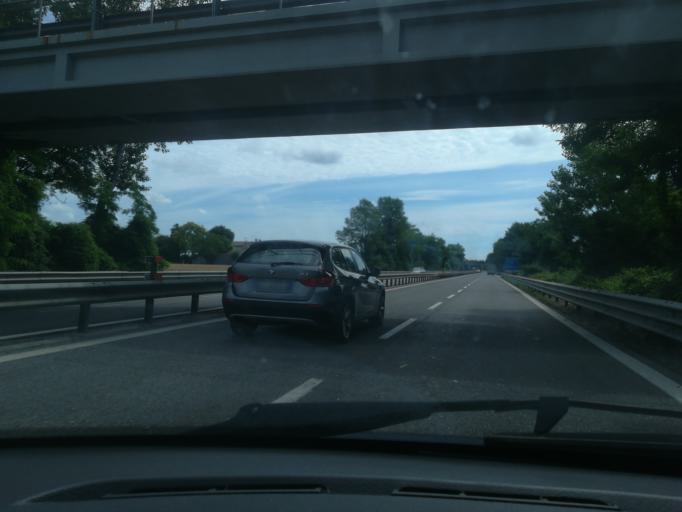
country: IT
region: The Marches
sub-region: Provincia di Macerata
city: Villa San Filippo
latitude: 43.2630
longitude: 13.5740
